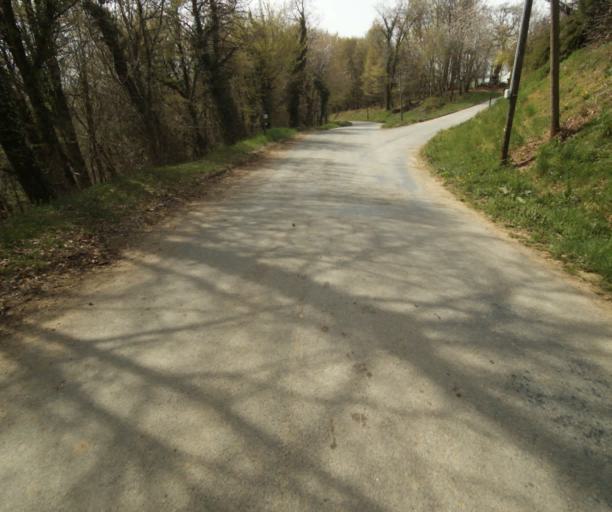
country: FR
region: Limousin
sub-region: Departement de la Correze
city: Naves
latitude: 45.3204
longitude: 1.7724
